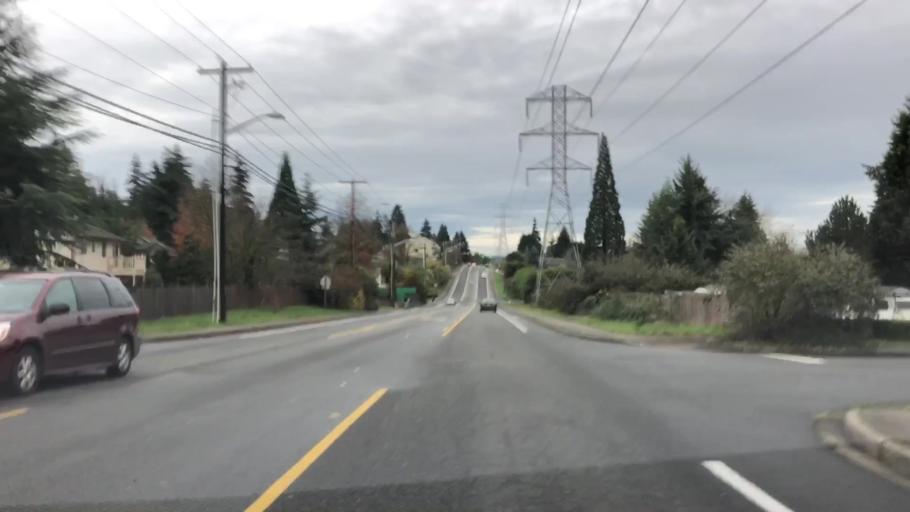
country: US
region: Washington
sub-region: King County
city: Kingsgate
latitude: 47.7229
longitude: -122.1755
